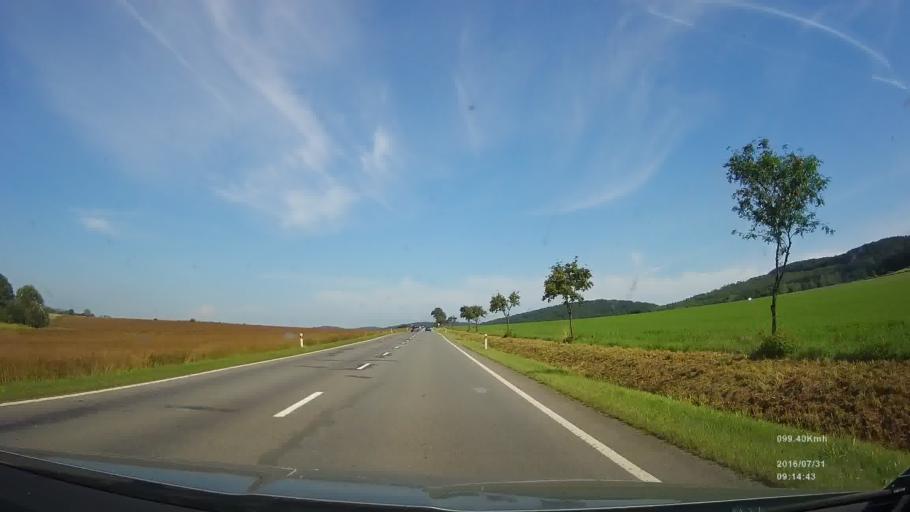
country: SK
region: Presovsky
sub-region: Okres Bardejov
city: Bardejov
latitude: 49.2248
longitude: 21.2901
